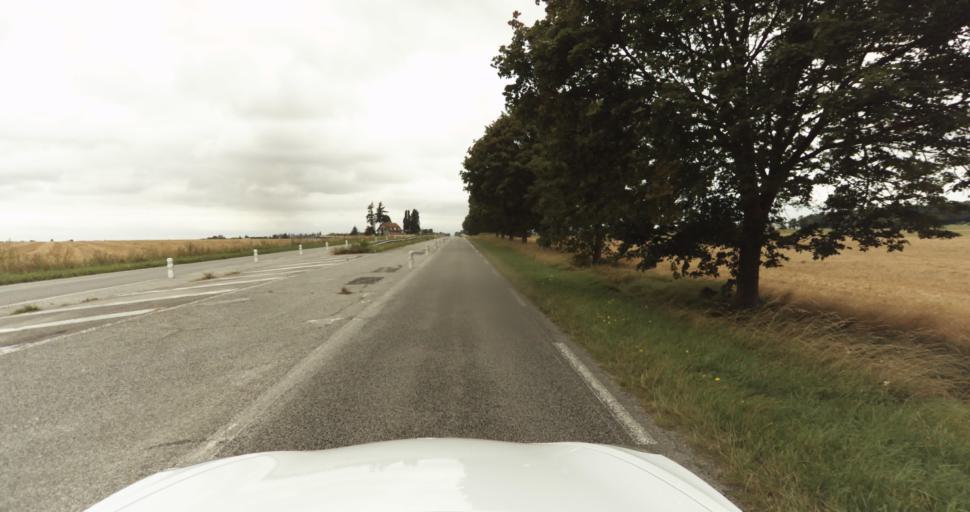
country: FR
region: Haute-Normandie
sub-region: Departement de l'Eure
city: Aviron
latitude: 49.0285
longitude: 1.1049
